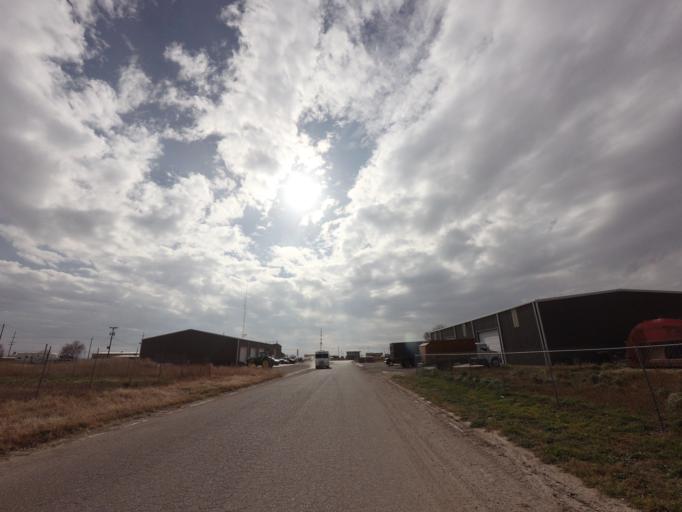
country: US
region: New Mexico
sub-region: Curry County
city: Clovis
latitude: 34.3916
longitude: -103.2167
